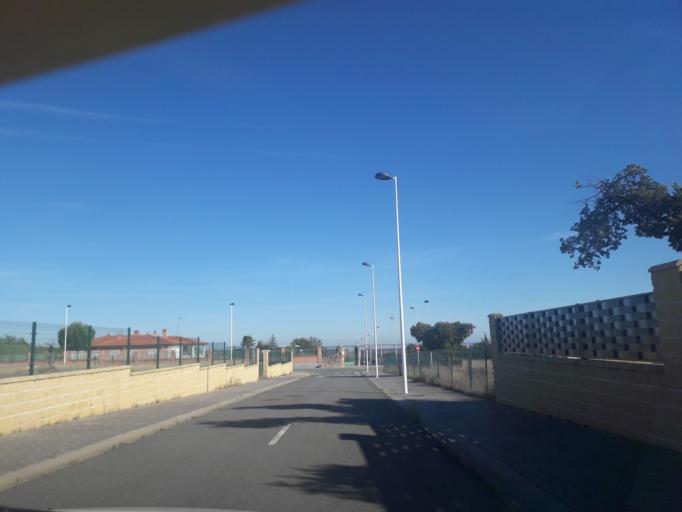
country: ES
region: Castille and Leon
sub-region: Provincia de Salamanca
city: Martinamor
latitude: 40.8060
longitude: -5.6480
